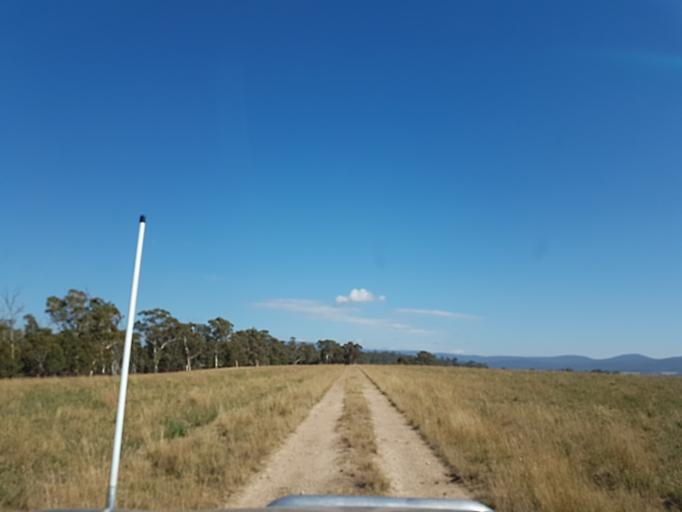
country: AU
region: New South Wales
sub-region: Snowy River
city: Jindabyne
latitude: -37.0461
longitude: 148.2873
